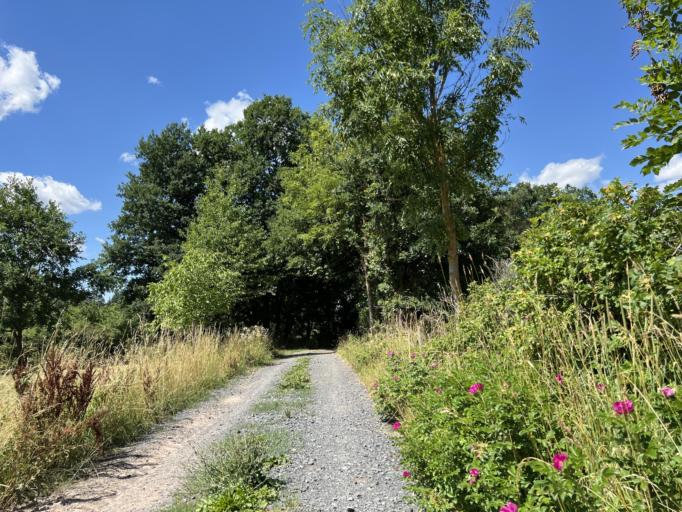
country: DE
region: Hesse
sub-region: Regierungsbezirk Darmstadt
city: Steinau an der Strasse
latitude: 50.2997
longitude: 9.4757
